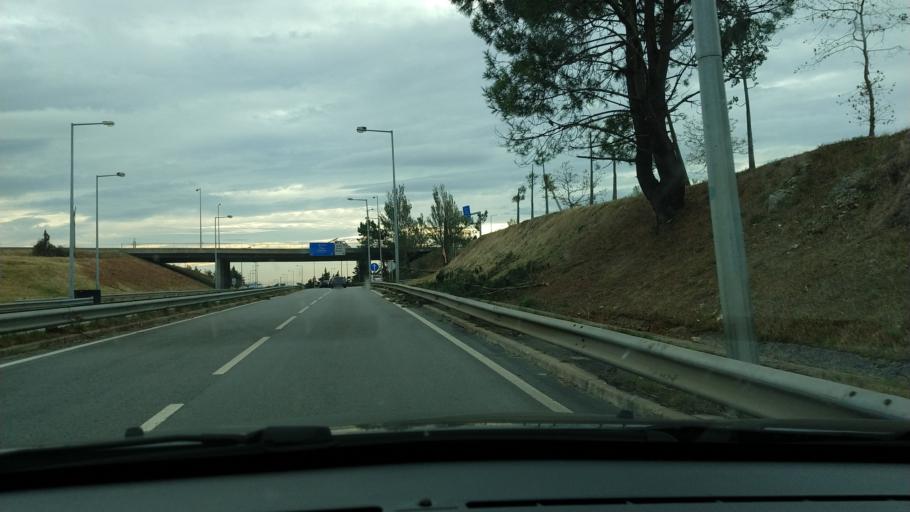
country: PT
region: Coimbra
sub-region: Figueira da Foz
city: Figueira da Foz
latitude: 40.1521
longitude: -8.8432
